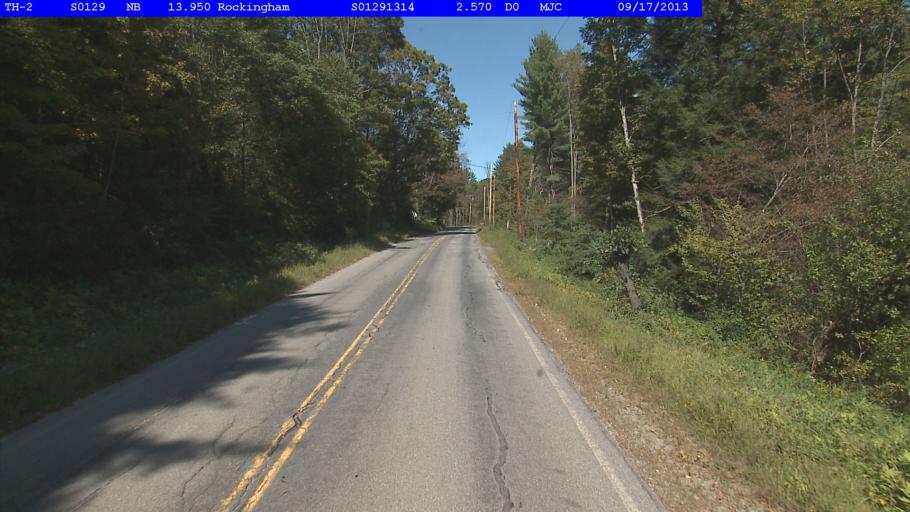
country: US
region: Vermont
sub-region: Windham County
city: Rockingham
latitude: 43.1544
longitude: -72.5175
